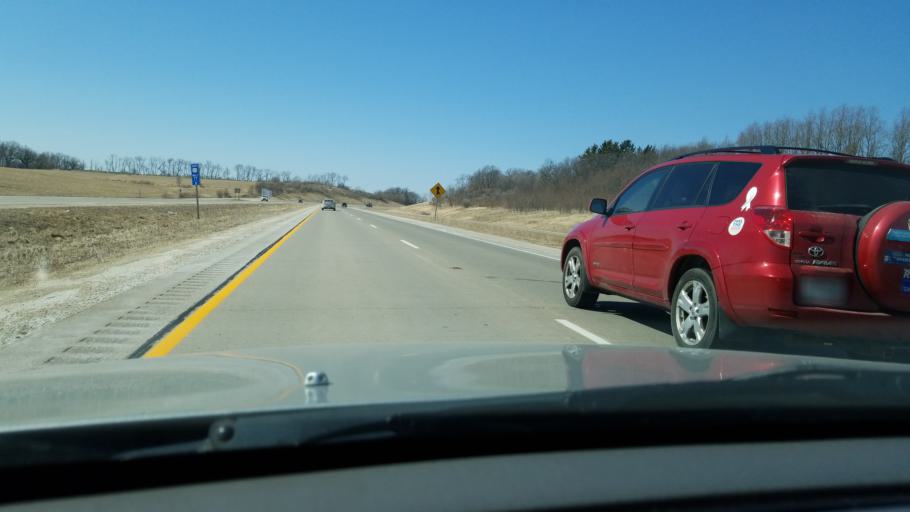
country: US
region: Wisconsin
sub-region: Dane County
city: Verona
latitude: 42.9749
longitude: -89.5473
